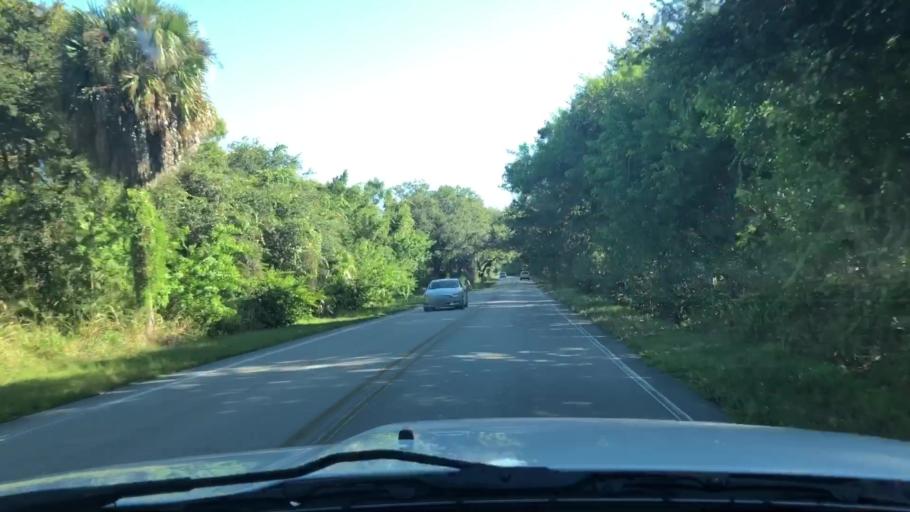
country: US
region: Florida
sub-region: Indian River County
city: Florida Ridge
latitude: 27.5751
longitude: -80.3759
